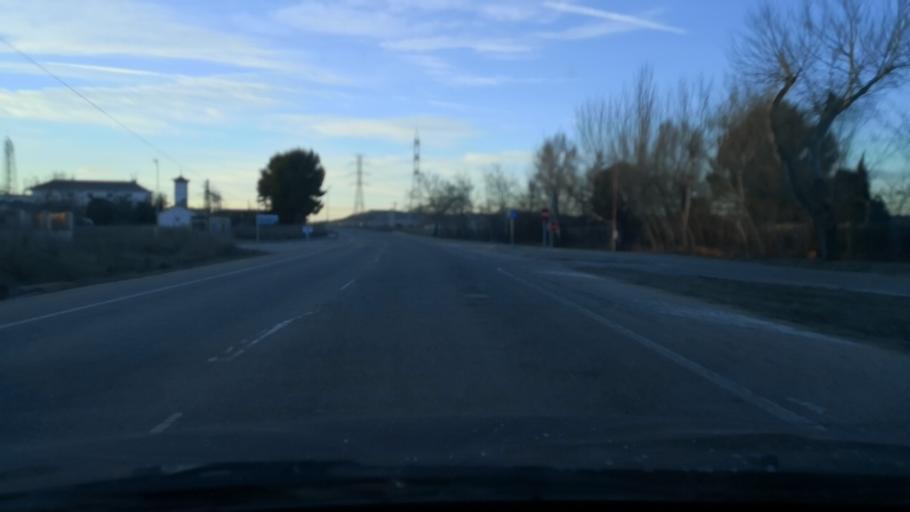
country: ES
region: Castille and Leon
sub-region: Provincia de Valladolid
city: Tordesillas
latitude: 41.5056
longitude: -5.0086
